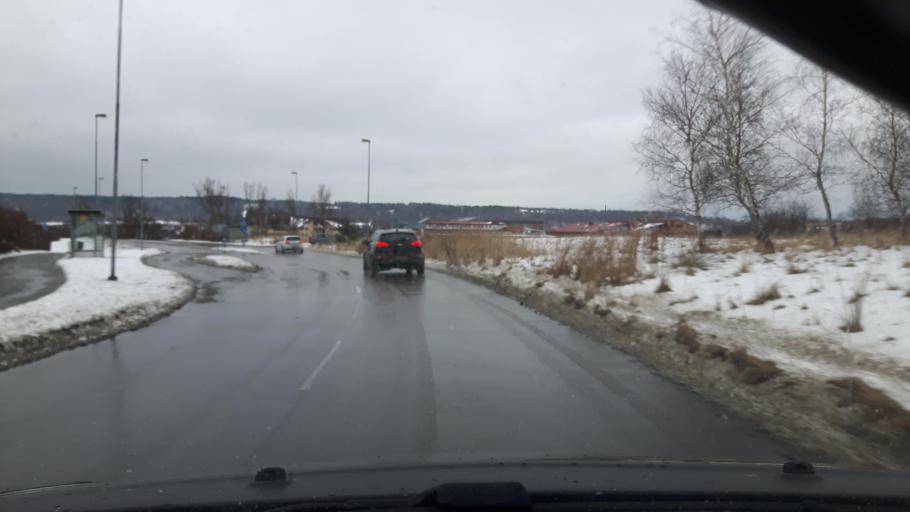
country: SE
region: Vaestra Goetaland
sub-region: Molndal
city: Moelndal
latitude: 57.6525
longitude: 11.9593
